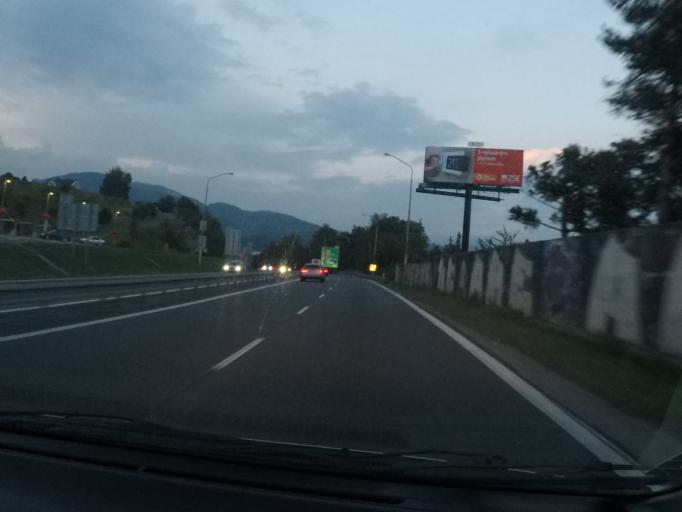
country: SK
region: Banskobystricky
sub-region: Okres Banska Bystrica
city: Banska Bystrica
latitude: 48.7413
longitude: 19.1366
